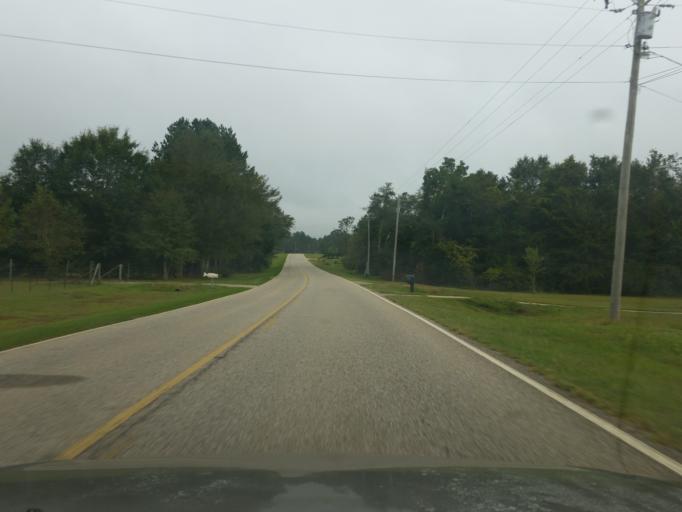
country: US
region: Florida
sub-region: Escambia County
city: Cantonment
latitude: 30.6394
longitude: -87.4433
